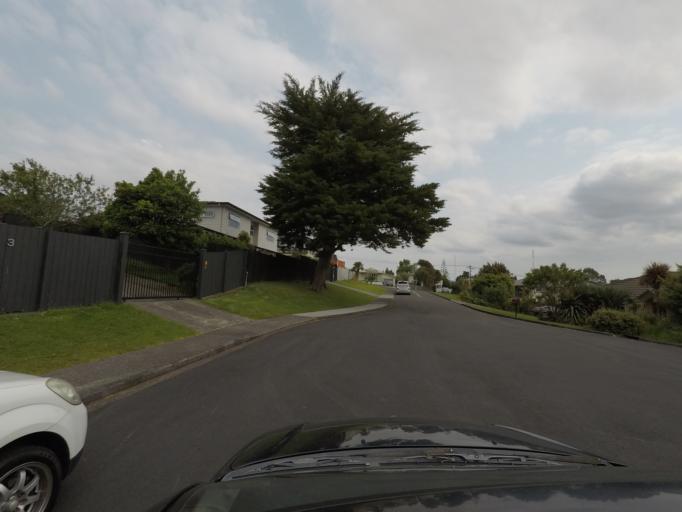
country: NZ
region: Auckland
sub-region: Auckland
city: Rosebank
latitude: -36.8380
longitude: 174.6394
